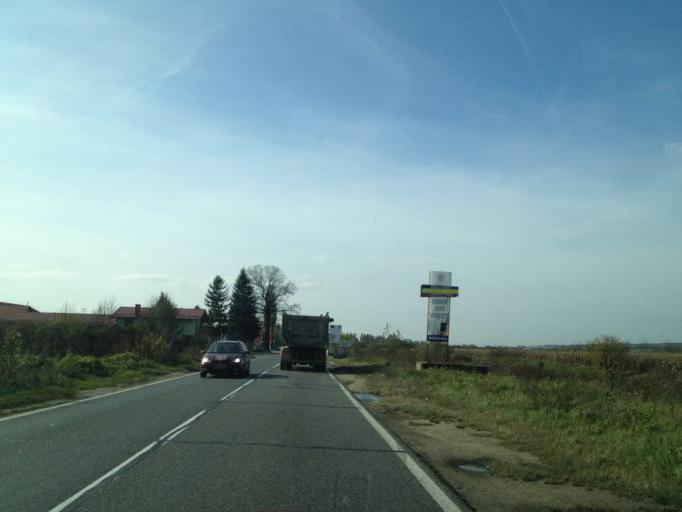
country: RO
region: Timis
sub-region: Comuna Faget
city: Faget
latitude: 45.8581
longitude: 22.1956
